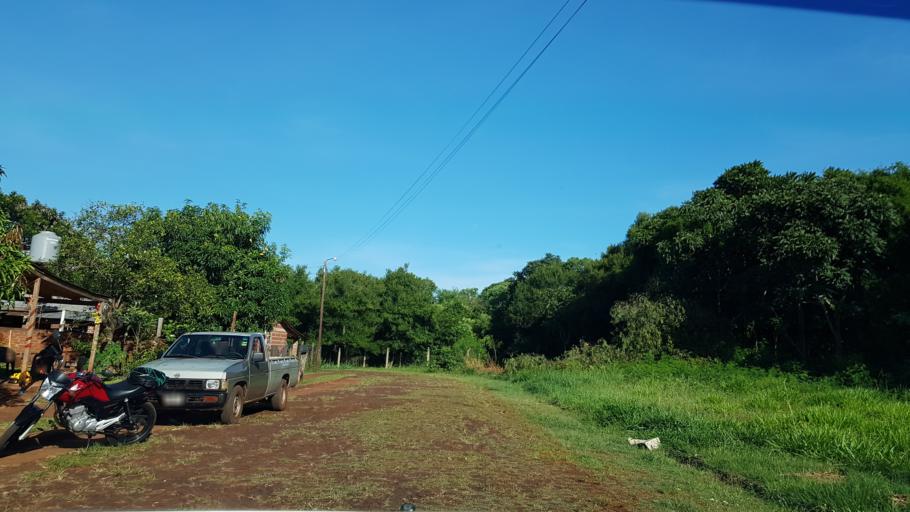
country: AR
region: Misiones
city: Puerto Libertad
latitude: -25.9235
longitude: -54.5788
